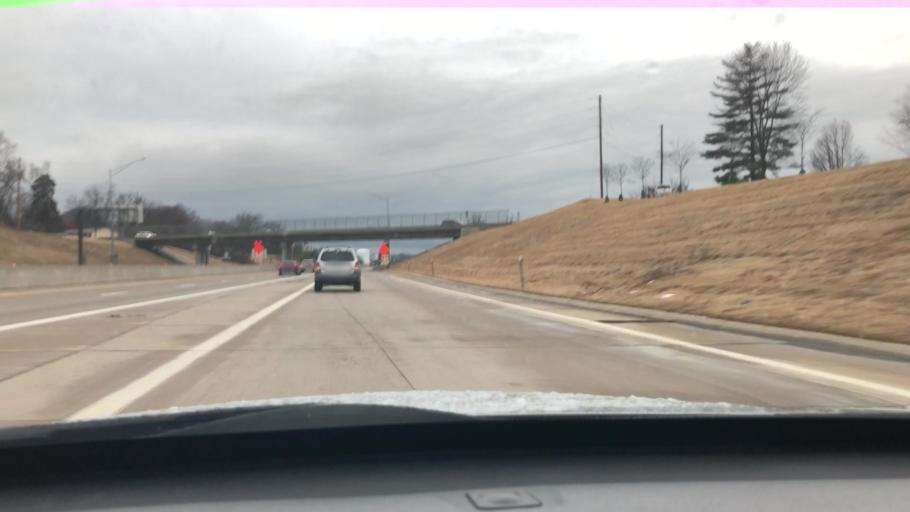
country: US
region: Missouri
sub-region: Saint Louis County
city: Valley Park
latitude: 38.5651
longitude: -90.4987
